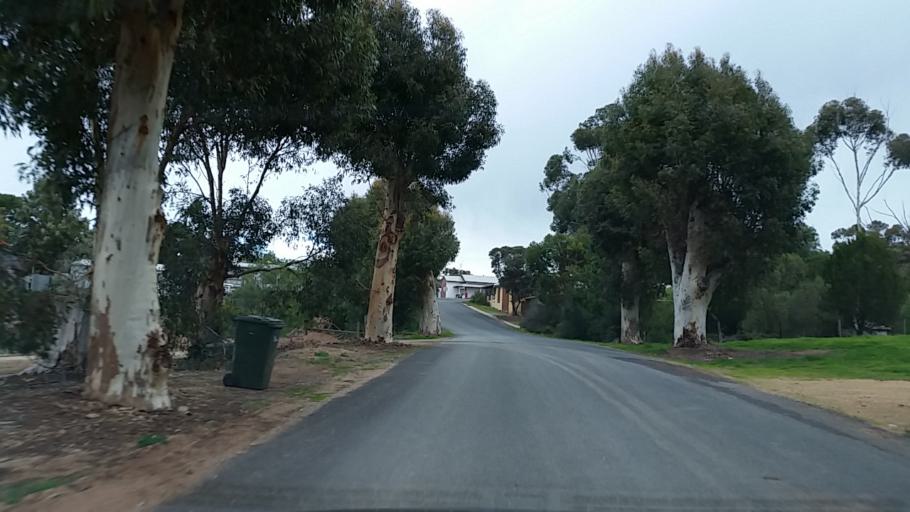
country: AU
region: South Australia
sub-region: Mid Murray
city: Mannum
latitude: -34.8510
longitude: 139.1602
